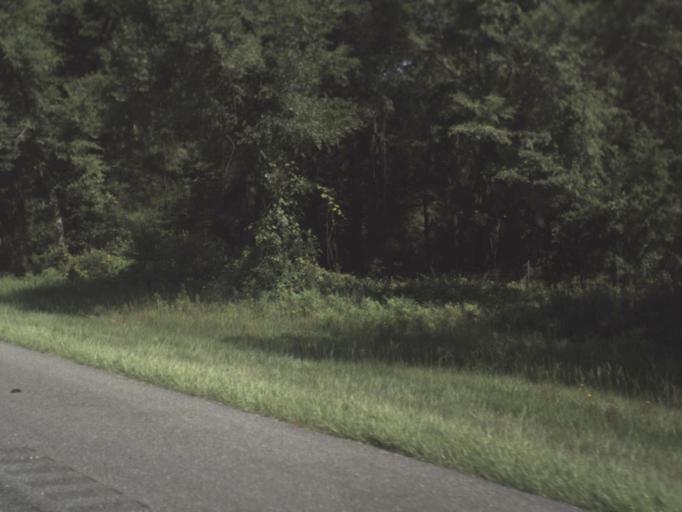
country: US
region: Florida
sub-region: Suwannee County
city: Live Oak
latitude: 30.3519
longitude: -83.1634
